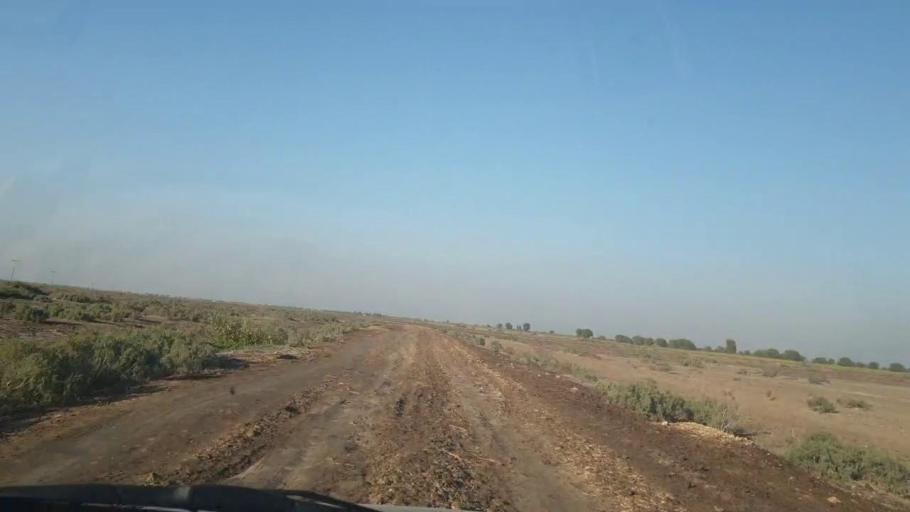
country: PK
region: Sindh
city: Mirpur Khas
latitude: 25.4356
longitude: 69.1003
